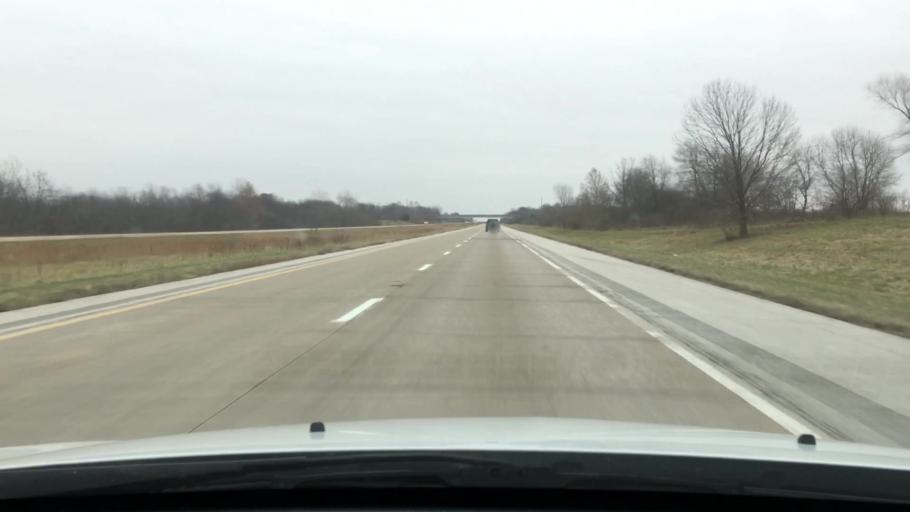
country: US
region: Illinois
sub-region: Scott County
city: Winchester
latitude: 39.6810
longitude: -90.5127
